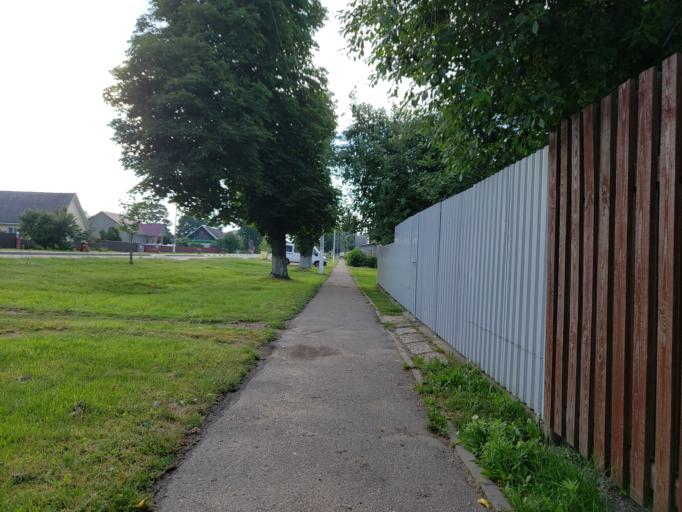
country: BY
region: Minsk
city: Chervyen'
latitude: 53.7068
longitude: 28.4330
